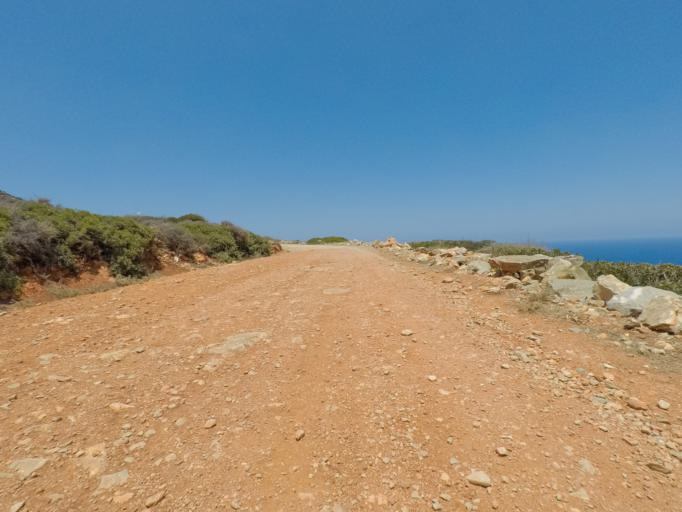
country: GR
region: Crete
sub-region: Nomos Lasithiou
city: Elounda
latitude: 35.3243
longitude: 25.7612
